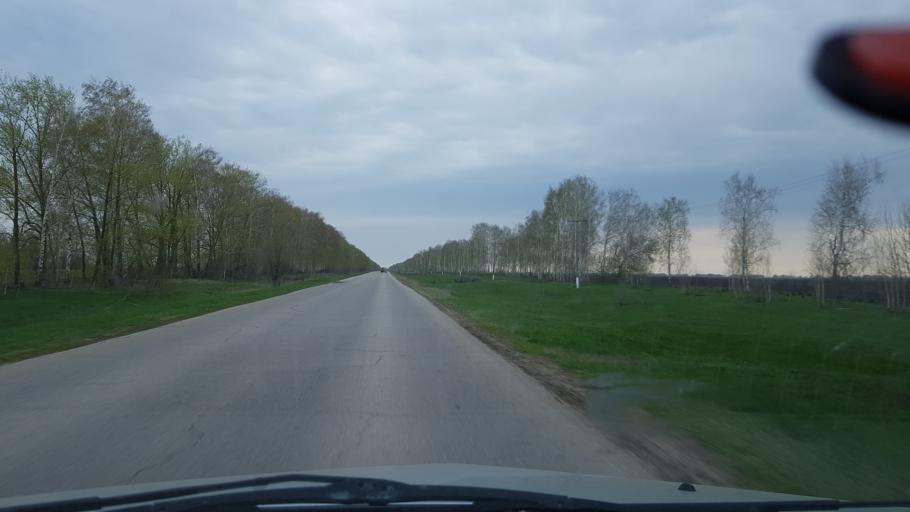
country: RU
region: Samara
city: Tol'yatti
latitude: 53.6589
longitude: 49.2362
